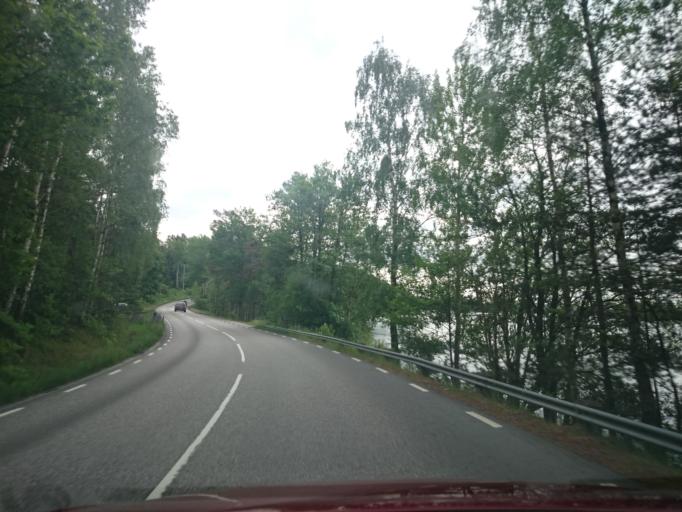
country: SE
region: Vaestra Goetaland
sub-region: Lerums Kommun
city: Stenkullen
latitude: 57.7434
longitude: 12.3373
